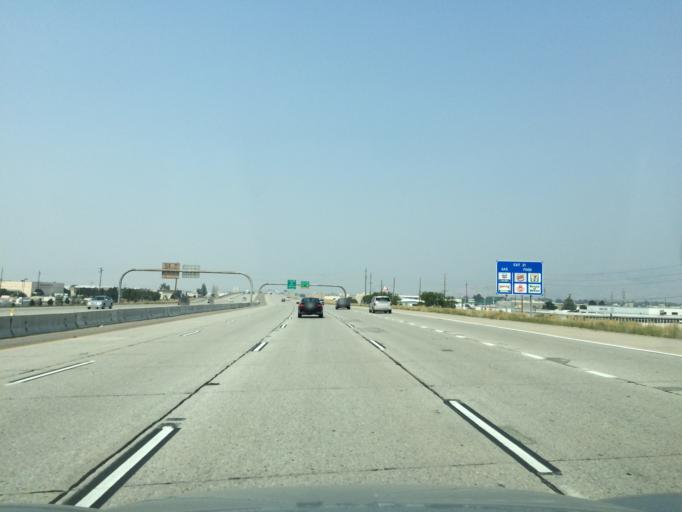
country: US
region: Utah
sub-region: Salt Lake County
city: South Salt Lake
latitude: 40.7340
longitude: -111.9493
